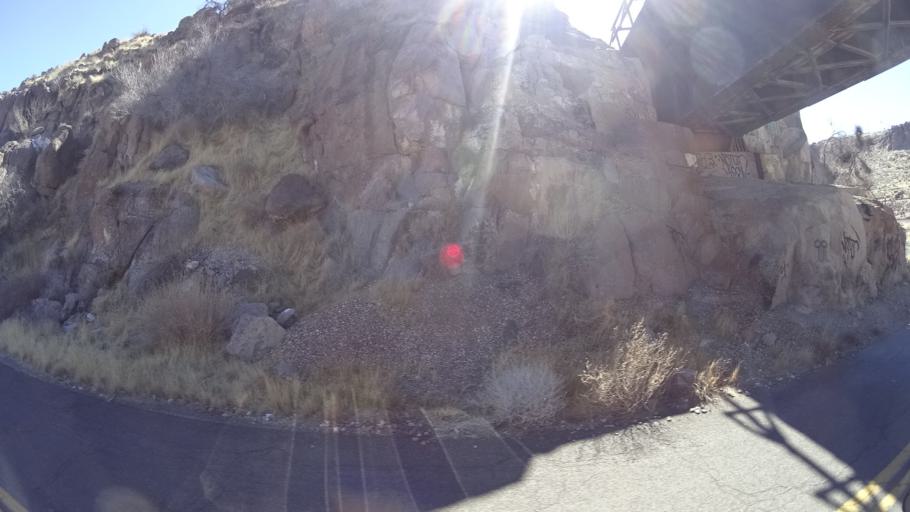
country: US
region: Arizona
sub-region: Mohave County
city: Kingman
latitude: 35.1821
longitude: -114.0621
